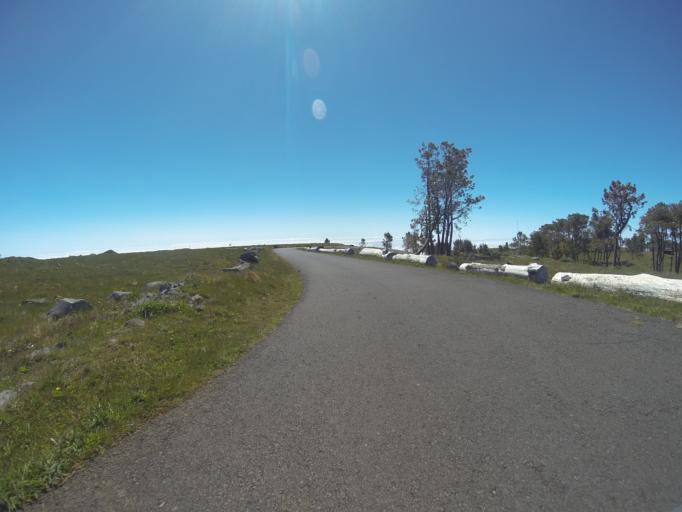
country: PT
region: Madeira
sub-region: Funchal
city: Nossa Senhora do Monte
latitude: 32.7155
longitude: -16.9106
